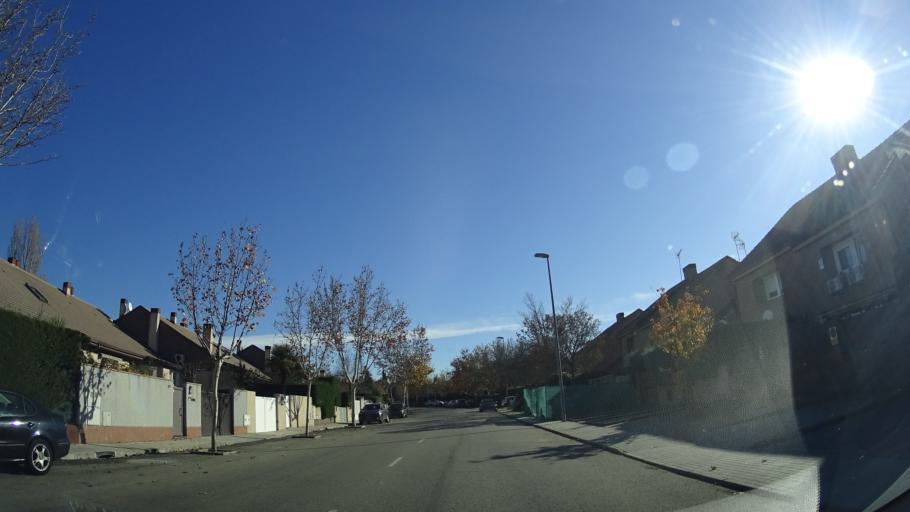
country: ES
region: Madrid
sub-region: Provincia de Madrid
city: Las Matas
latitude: 40.5213
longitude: -3.9109
